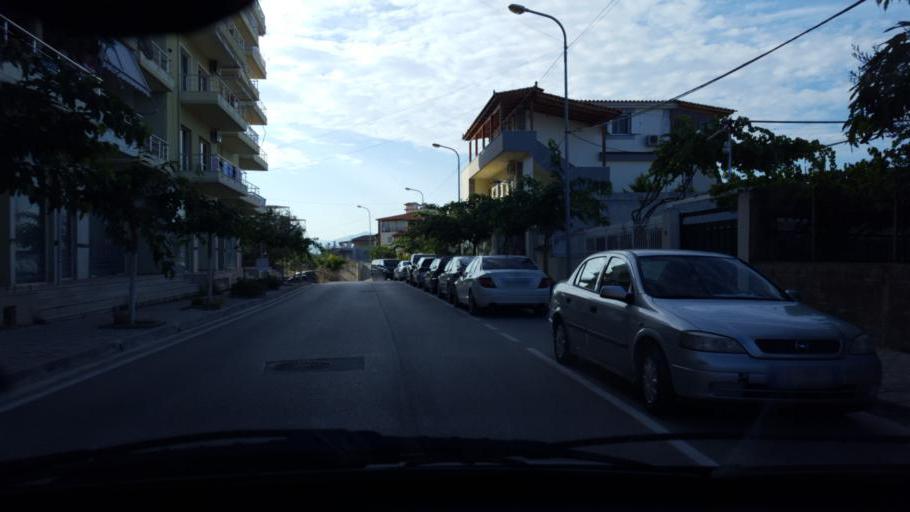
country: AL
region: Vlore
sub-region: Rrethi i Sarandes
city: Sarande
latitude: 39.8730
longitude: 19.9914
